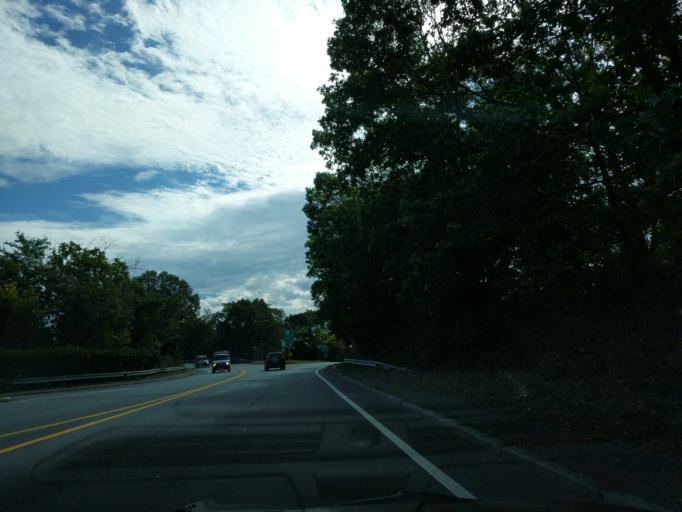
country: US
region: Massachusetts
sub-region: Essex County
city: Saugus
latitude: 42.4583
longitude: -71.0261
